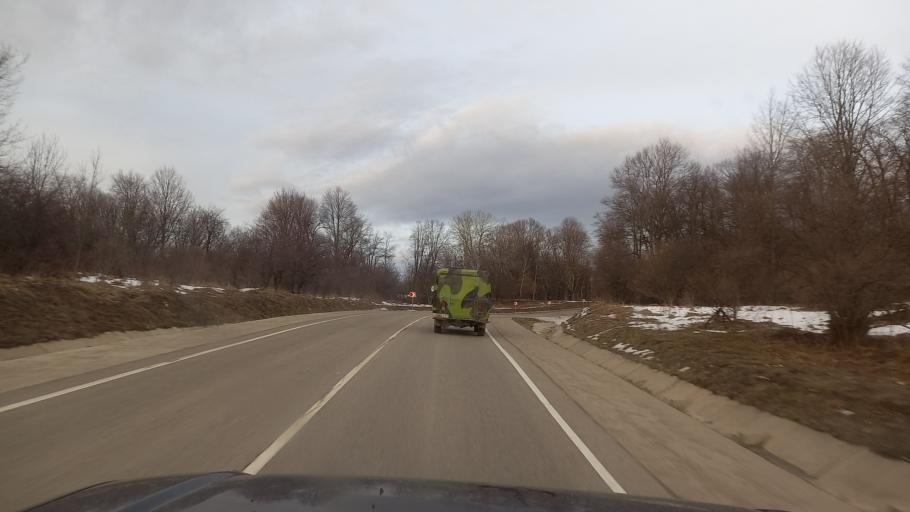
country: RU
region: Adygeya
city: Kamennomostskiy
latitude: 44.2211
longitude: 39.9797
